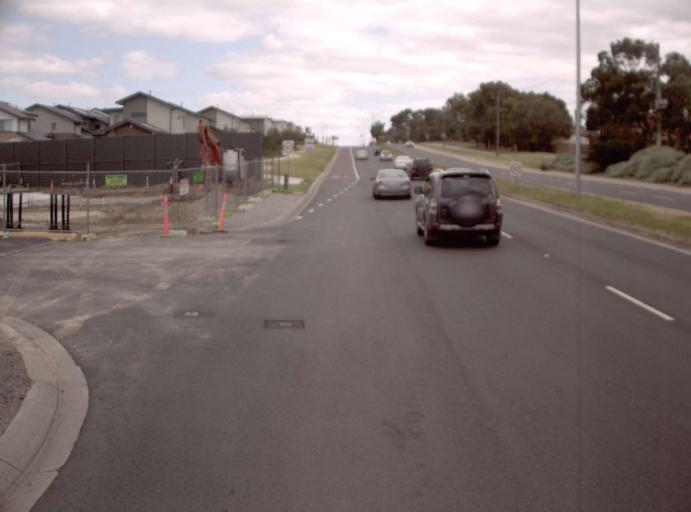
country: AU
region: Victoria
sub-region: Knox
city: Wantirna South
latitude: -37.8781
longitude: 145.2331
